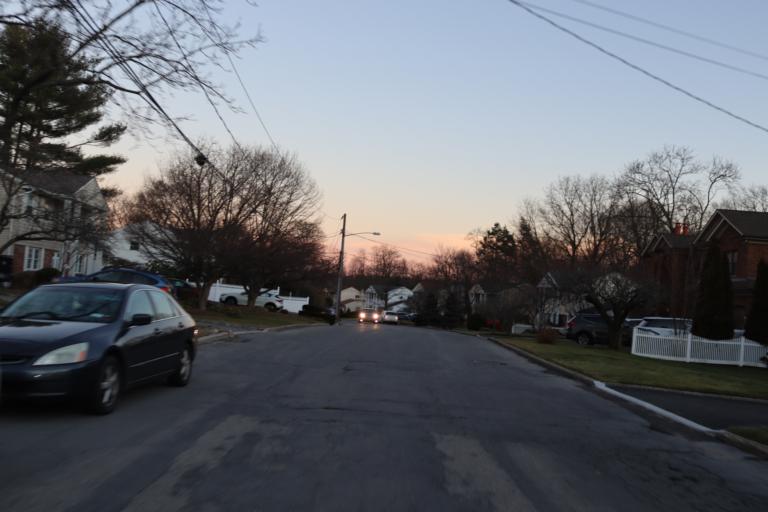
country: US
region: New York
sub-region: Nassau County
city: Glen Cove
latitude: 40.8548
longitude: -73.6283
